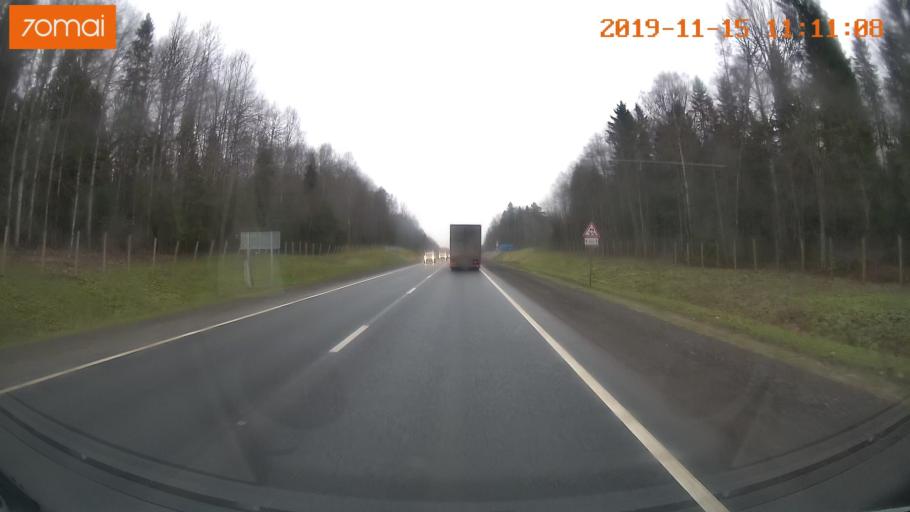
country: RU
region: Vologda
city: Chebsara
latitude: 59.1212
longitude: 39.1369
